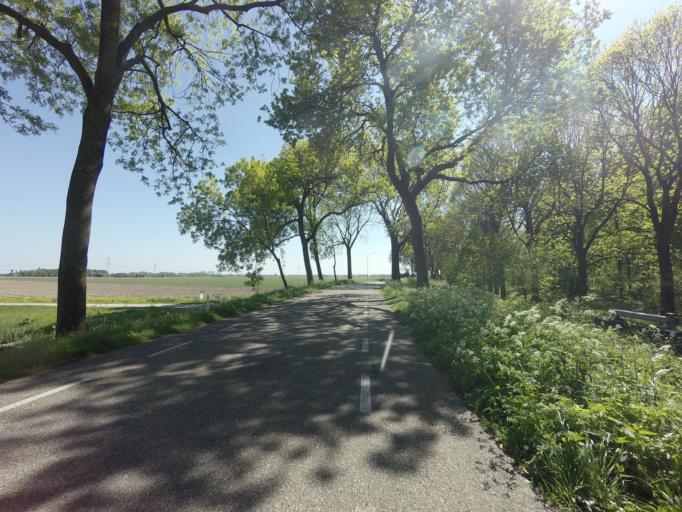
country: NL
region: North Brabant
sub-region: Gemeente Moerdijk
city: Klundert
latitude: 51.6759
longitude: 4.6198
